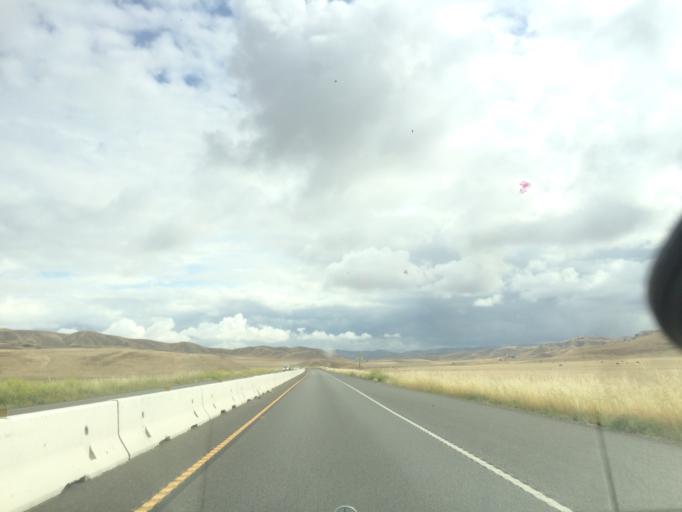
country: US
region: California
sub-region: San Luis Obispo County
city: Shandon
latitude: 35.6976
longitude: -120.3268
